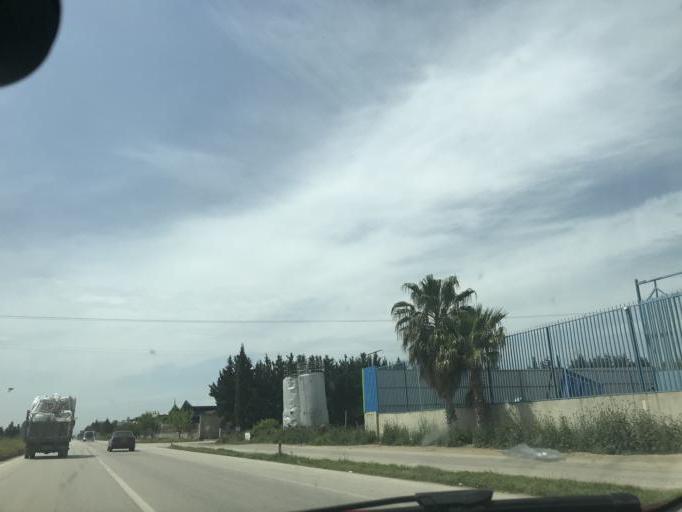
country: TR
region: Adana
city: Yakapinar
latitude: 36.9711
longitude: 35.5235
